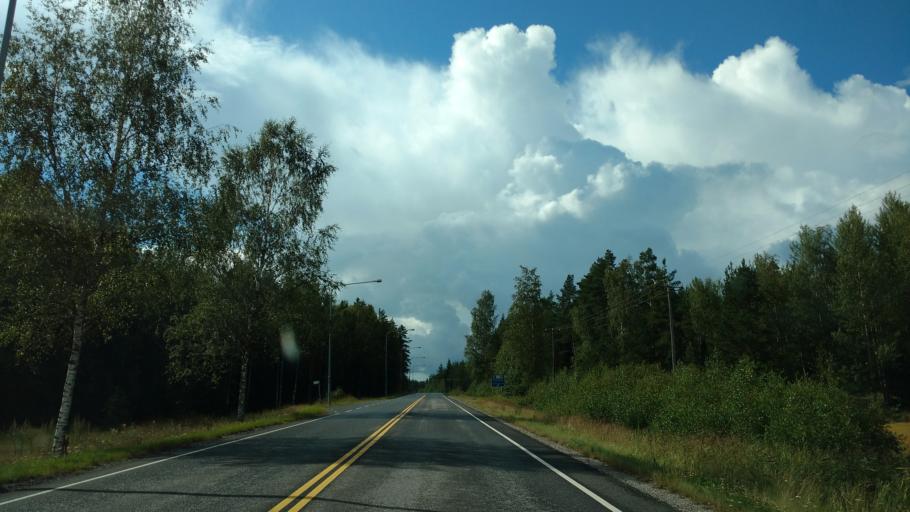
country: FI
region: Varsinais-Suomi
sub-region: Turku
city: Paimio
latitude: 60.4201
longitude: 22.7426
